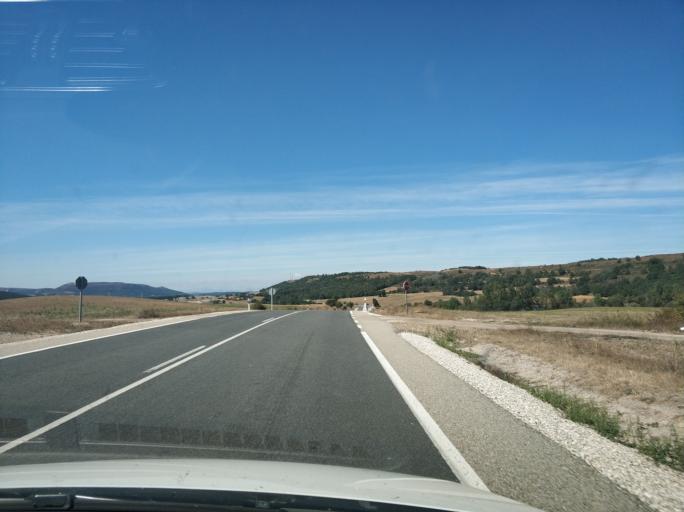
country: ES
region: Castille and Leon
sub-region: Provincia de Burgos
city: Basconcillos del Tozo
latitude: 42.6772
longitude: -3.9425
